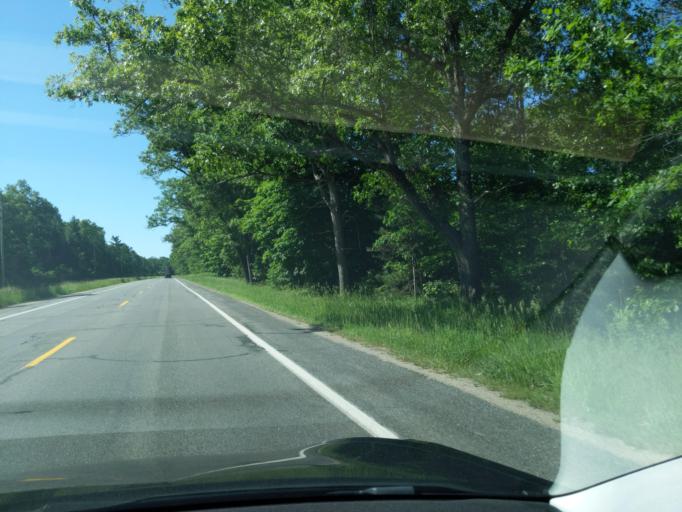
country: US
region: Michigan
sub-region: Muskegon County
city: Lakewood Club
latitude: 43.3750
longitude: -86.2839
